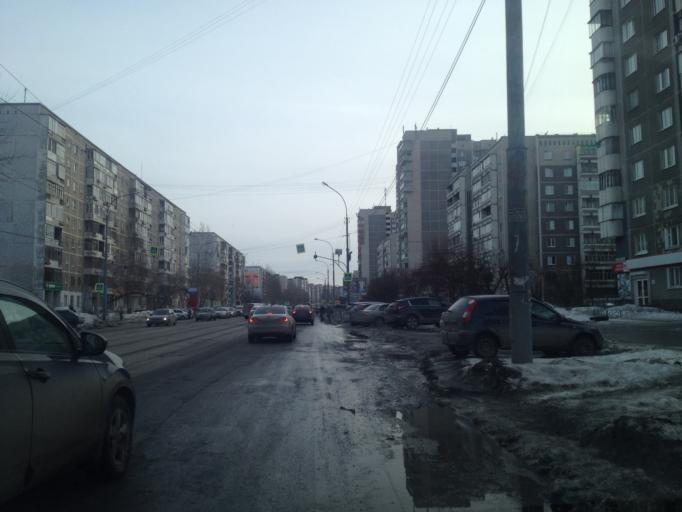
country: RU
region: Sverdlovsk
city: Yekaterinburg
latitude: 56.8344
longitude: 60.5454
